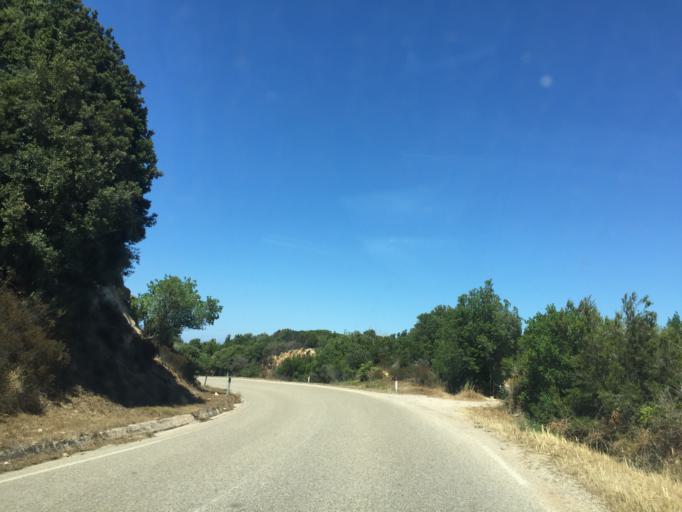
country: IT
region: Sardinia
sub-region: Provincia di Olbia-Tempio
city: Aglientu
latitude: 41.0880
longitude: 9.1184
